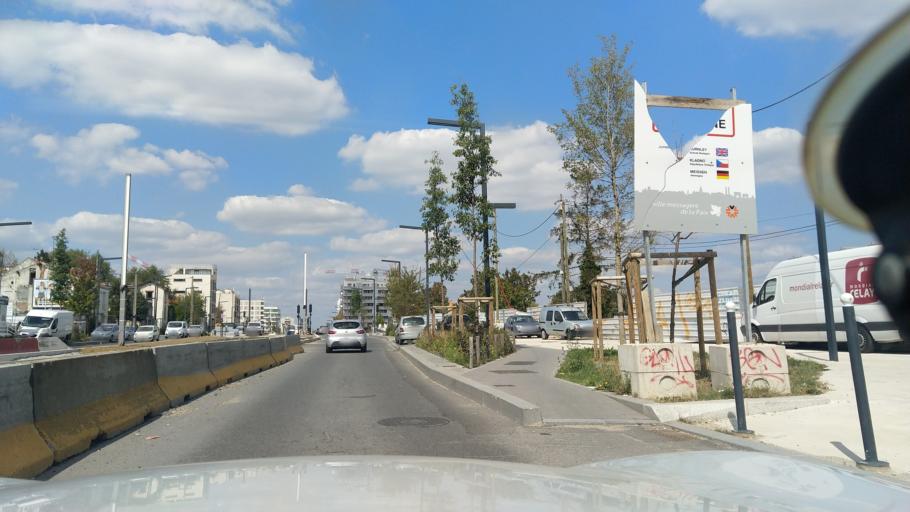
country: FR
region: Ile-de-France
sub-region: Departement du Val-de-Marne
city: Thiais
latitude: 48.7748
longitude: 2.3989
